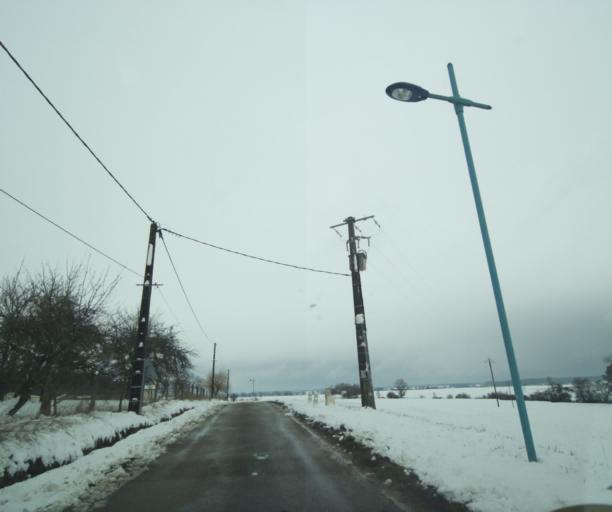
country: FR
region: Champagne-Ardenne
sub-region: Departement de la Haute-Marne
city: Montier-en-Der
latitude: 48.4238
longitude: 4.7888
